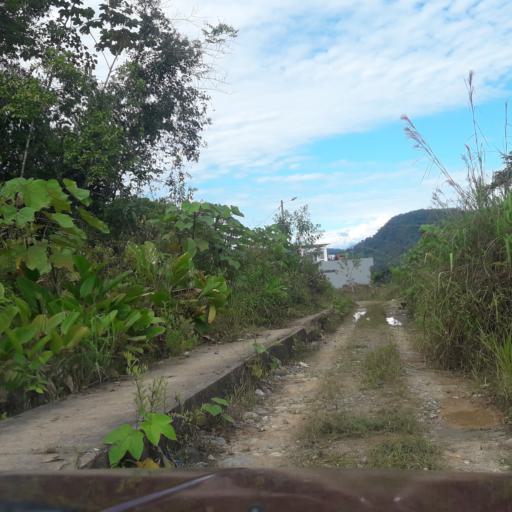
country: EC
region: Napo
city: Tena
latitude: -0.9816
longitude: -77.8255
